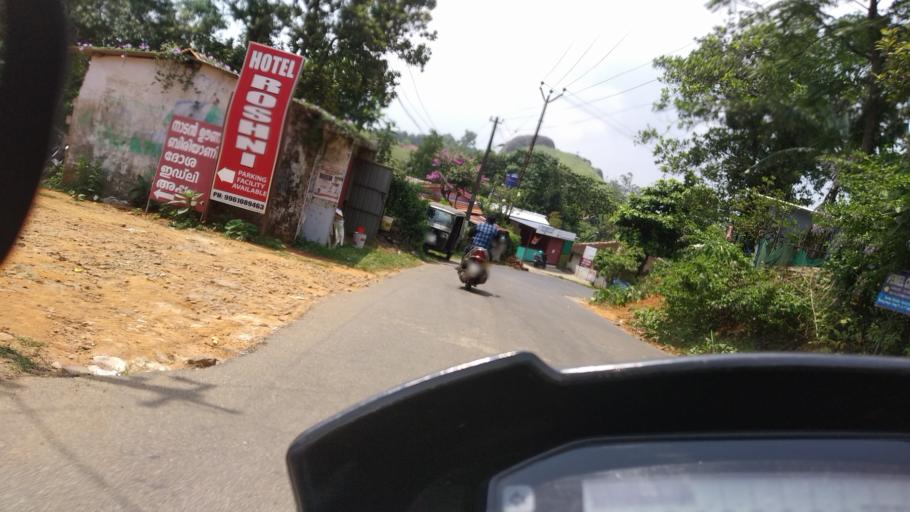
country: IN
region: Kerala
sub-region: Kottayam
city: Erattupetta
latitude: 9.6558
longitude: 76.9257
